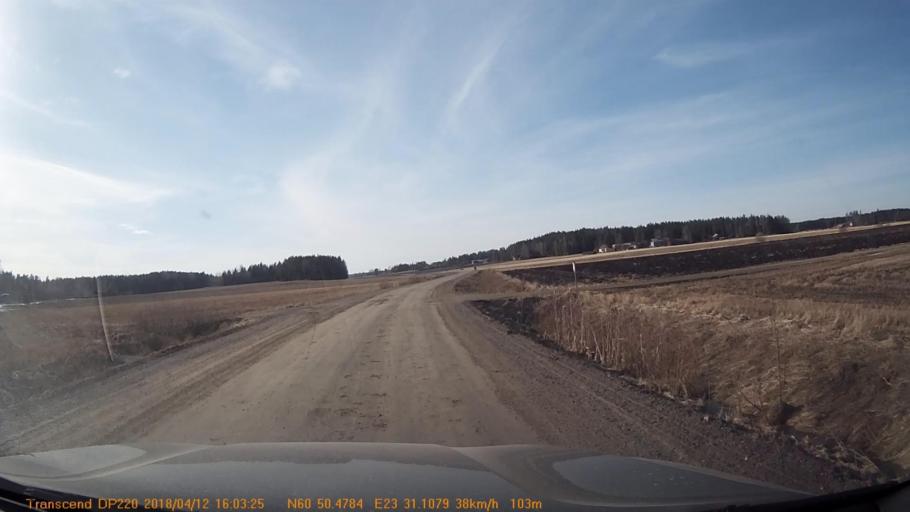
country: FI
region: Haeme
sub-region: Forssa
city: Jokioinen
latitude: 60.8414
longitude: 23.5181
